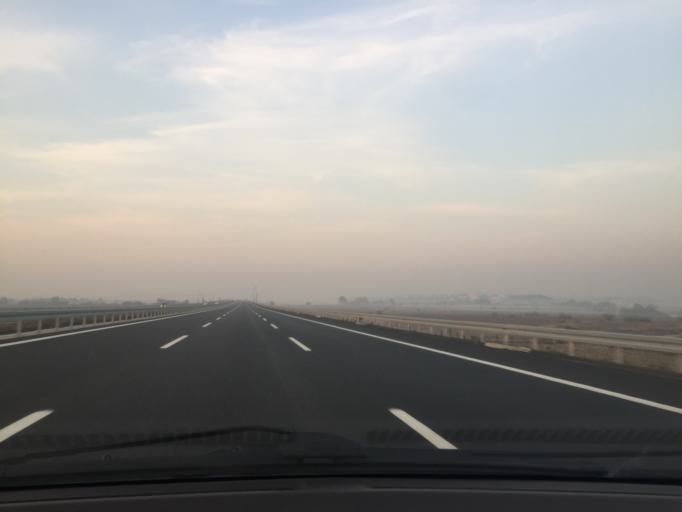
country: TR
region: Bursa
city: Karacabey
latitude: 40.2292
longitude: 28.4120
